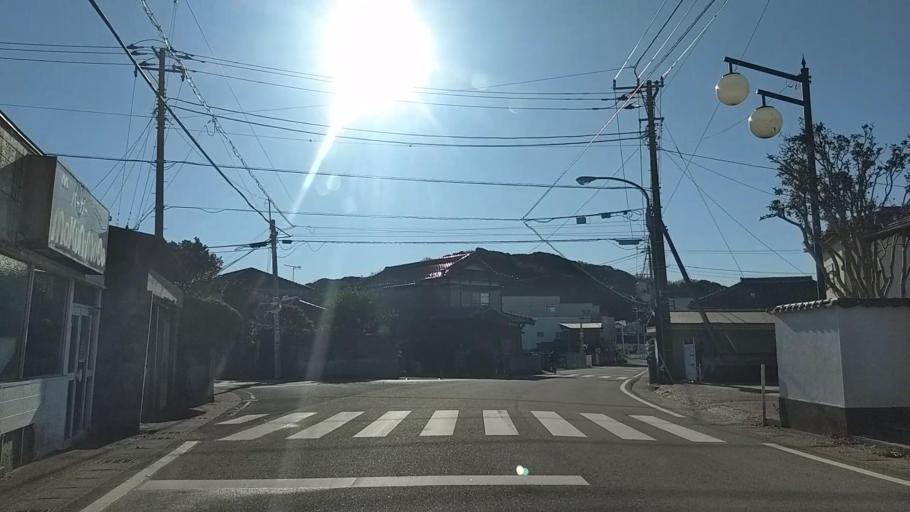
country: JP
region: Chiba
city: Futtsu
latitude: 35.2868
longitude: 139.8579
